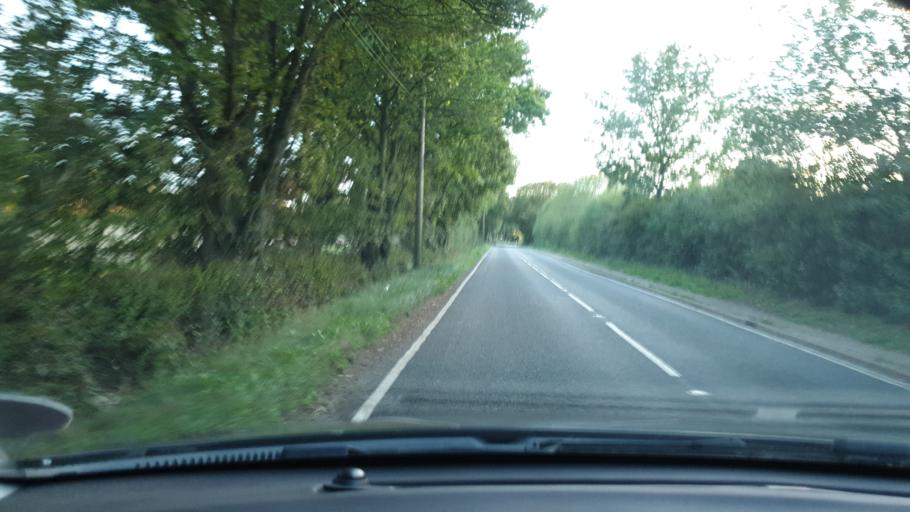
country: GB
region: England
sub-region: Essex
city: Wivenhoe
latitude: 51.8997
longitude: 0.9595
